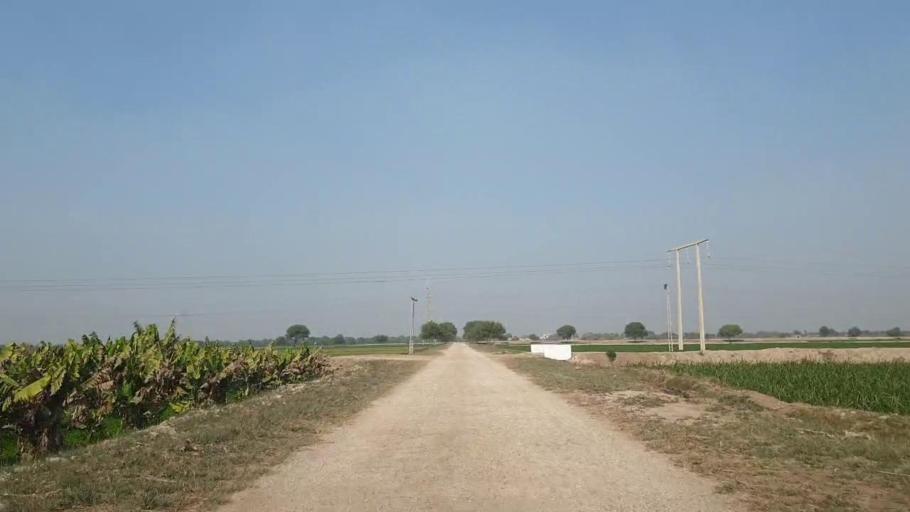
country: PK
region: Sindh
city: Tando Allahyar
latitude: 25.4971
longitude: 68.8340
